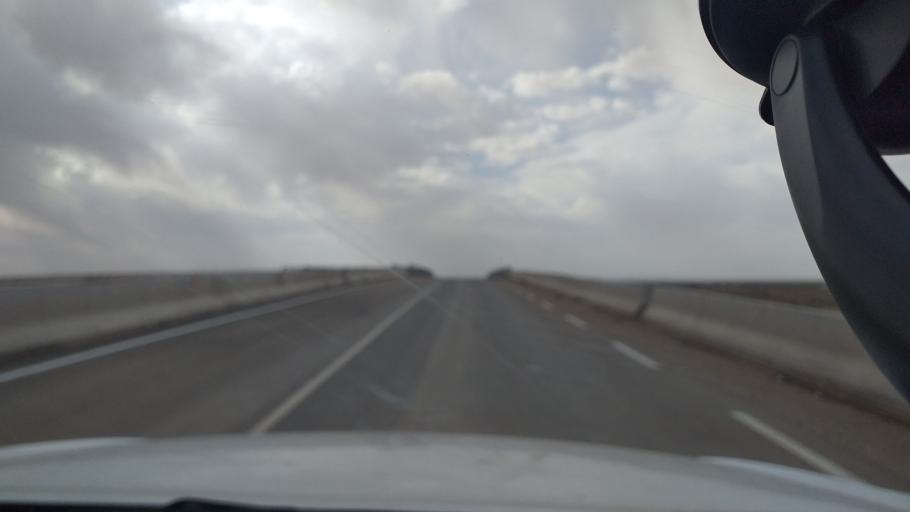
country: TN
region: Madanin
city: Medenine
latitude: 33.3011
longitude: 10.6099
